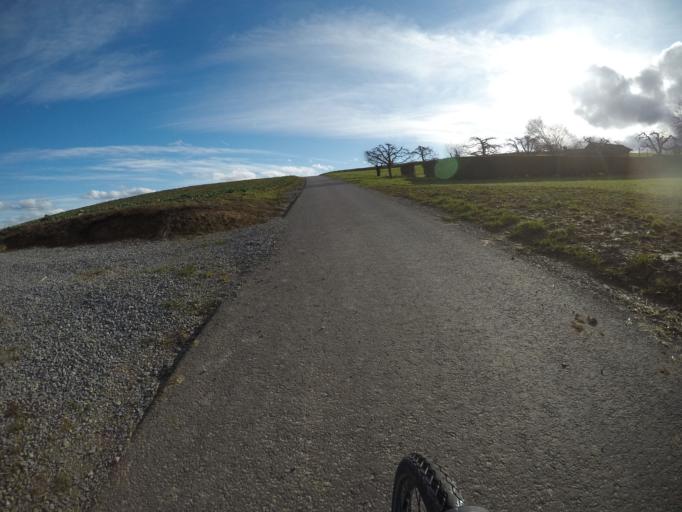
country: DE
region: Baden-Wuerttemberg
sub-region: Regierungsbezirk Stuttgart
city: Herrenberg
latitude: 48.5890
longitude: 8.8455
